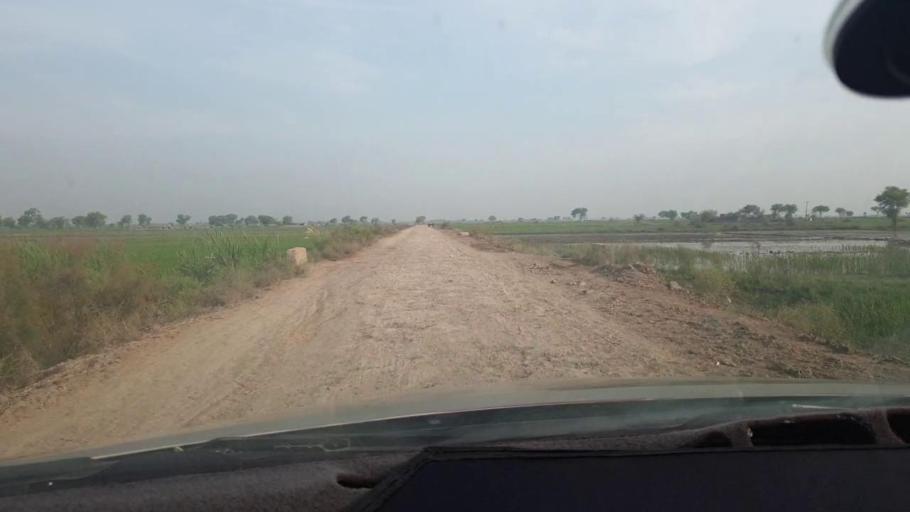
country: PK
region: Balochistan
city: Jhatpat
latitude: 28.3525
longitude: 68.4097
